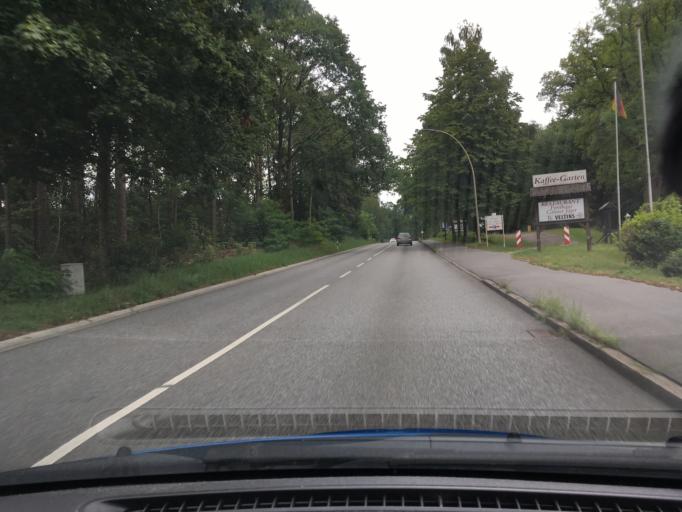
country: DE
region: Schleswig-Holstein
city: Hamwarde
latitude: 53.4244
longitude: 10.4152
